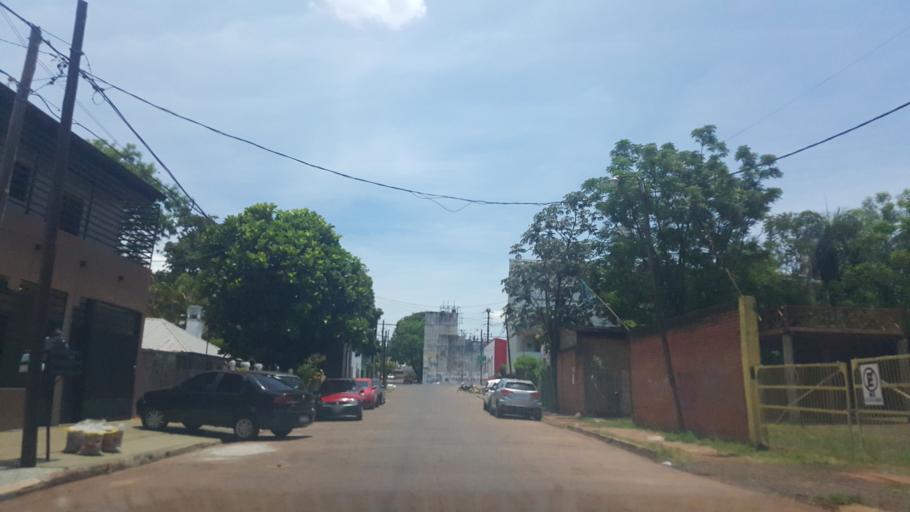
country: AR
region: Misiones
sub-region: Departamento de Capital
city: Posadas
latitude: -27.3752
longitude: -55.9014
